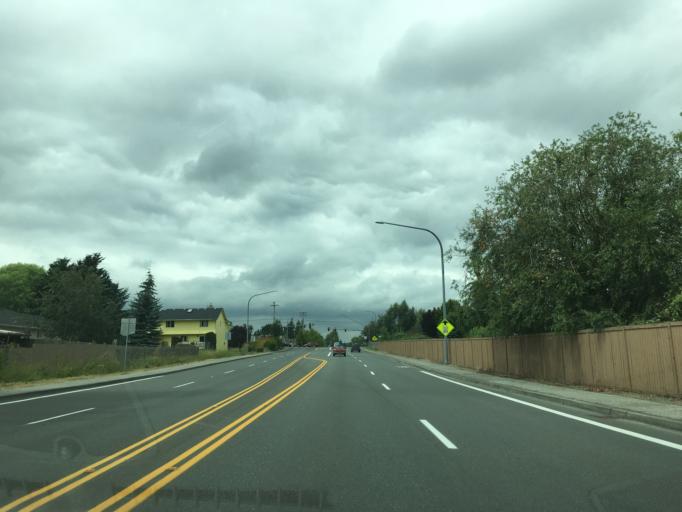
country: US
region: Washington
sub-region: Snohomish County
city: Marysville
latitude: 48.0744
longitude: -122.1372
